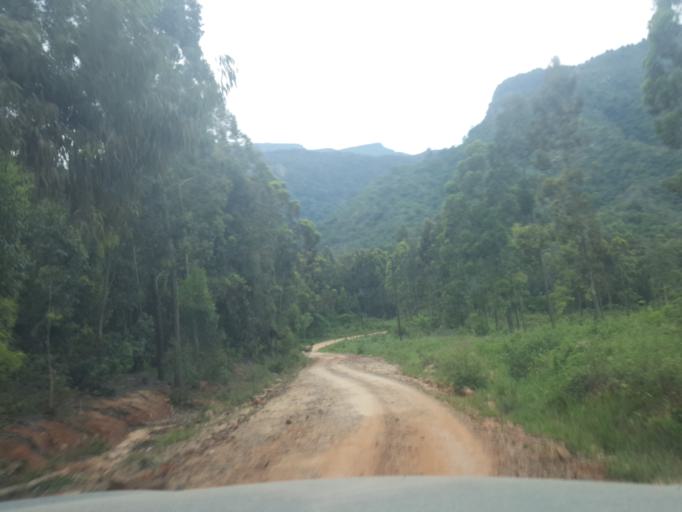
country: ZA
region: Limpopo
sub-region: Mopani District Municipality
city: Hoedspruit
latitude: -24.5937
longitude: 30.8813
